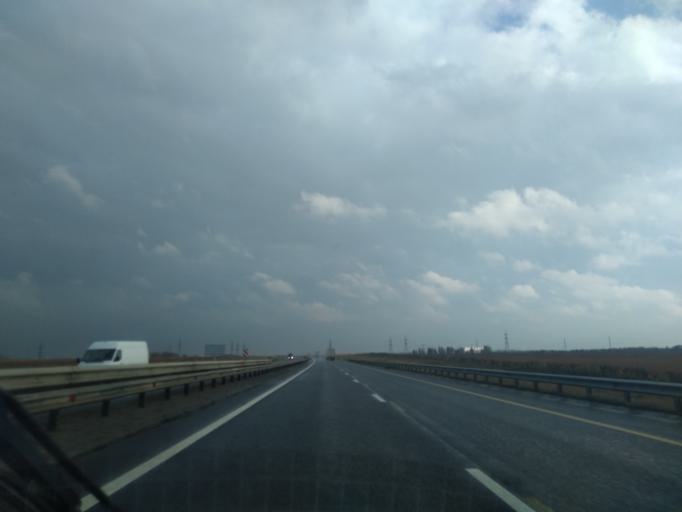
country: RU
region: Lipetsk
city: Yelets
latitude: 52.5908
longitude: 38.6768
